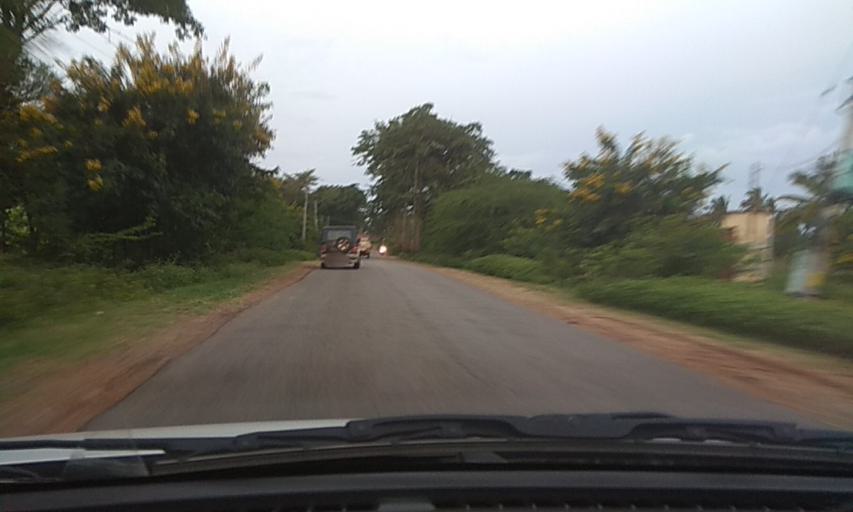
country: IN
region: Karnataka
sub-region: Chamrajnagar
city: Gundlupet
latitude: 11.8138
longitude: 76.7647
